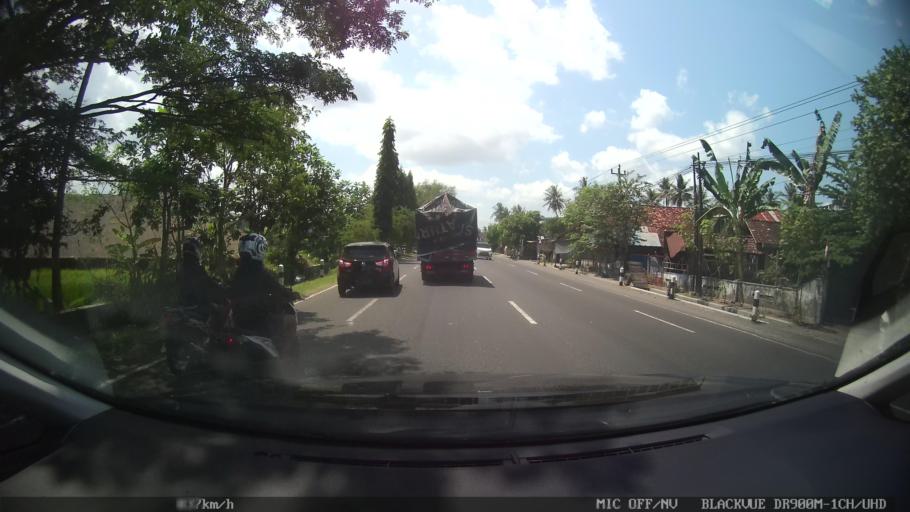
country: ID
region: Daerah Istimewa Yogyakarta
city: Pandak
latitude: -7.9117
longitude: 110.2909
